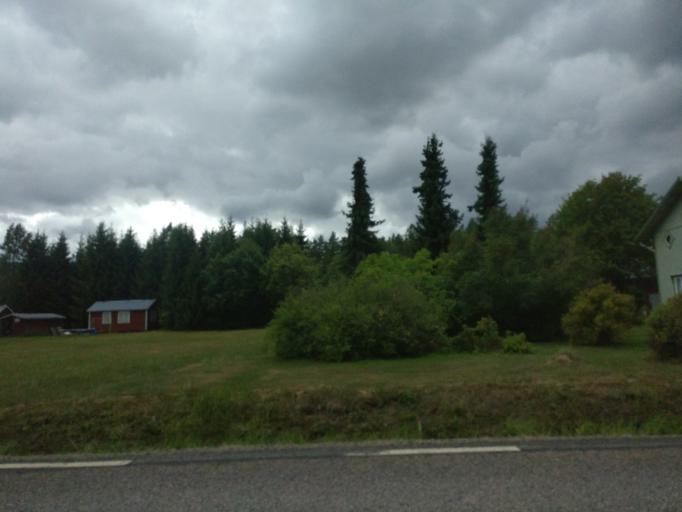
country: SE
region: Vaermland
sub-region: Torsby Kommun
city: Torsby
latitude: 60.7573
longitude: 12.7716
